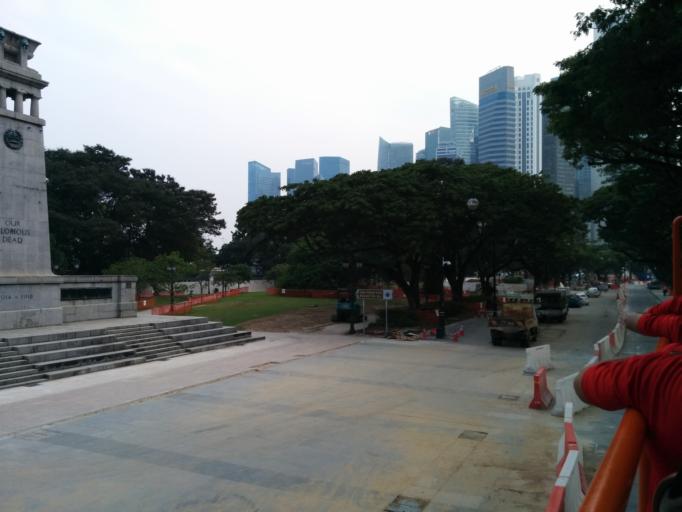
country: SG
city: Singapore
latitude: 1.2906
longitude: 103.8537
